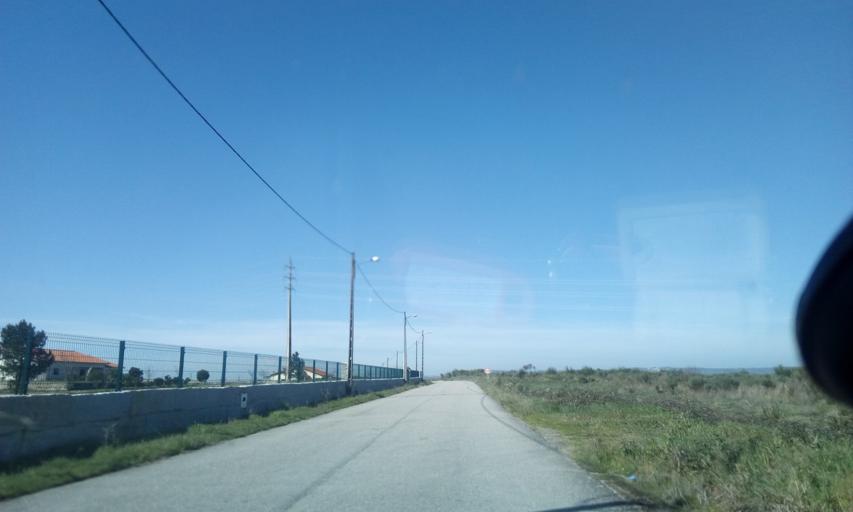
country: PT
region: Guarda
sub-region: Celorico da Beira
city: Celorico da Beira
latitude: 40.5922
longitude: -7.4427
